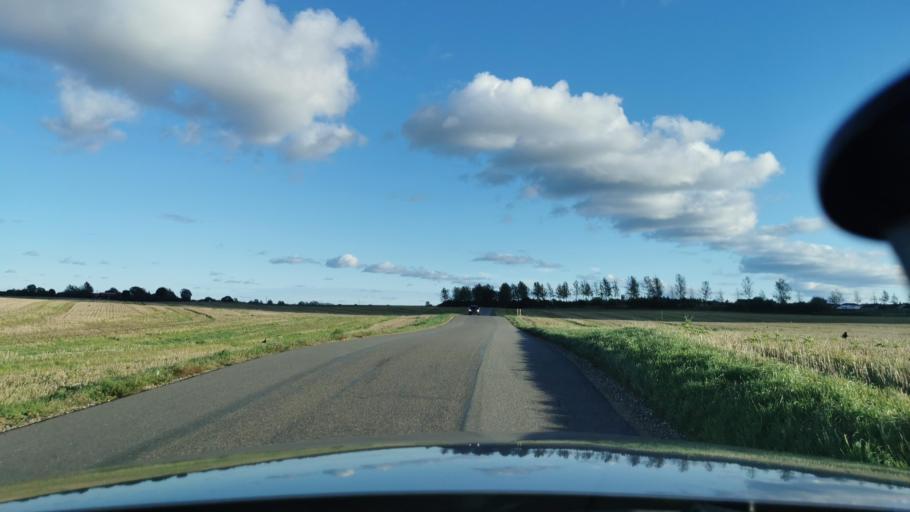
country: DK
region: Capital Region
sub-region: Hoje-Taastrup Kommune
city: Flong
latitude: 55.6662
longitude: 12.1465
